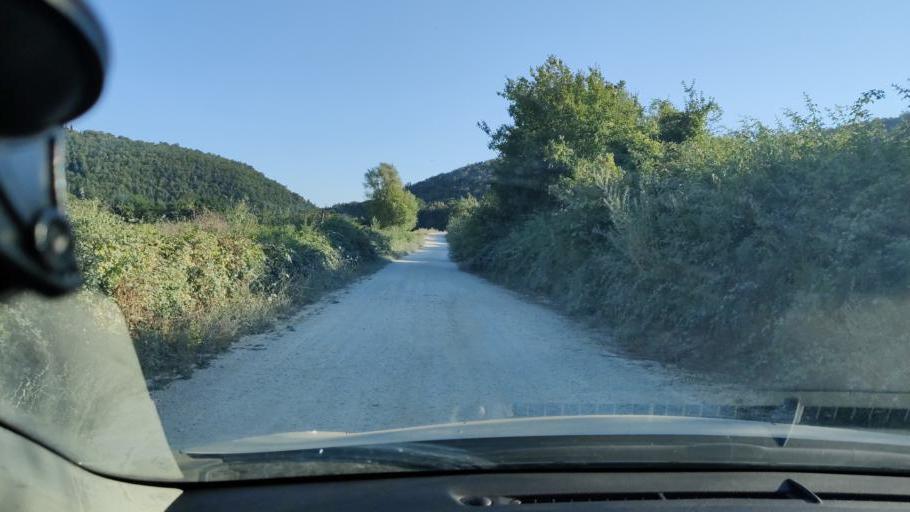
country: IT
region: Umbria
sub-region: Provincia di Terni
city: Amelia
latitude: 42.5428
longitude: 12.3864
